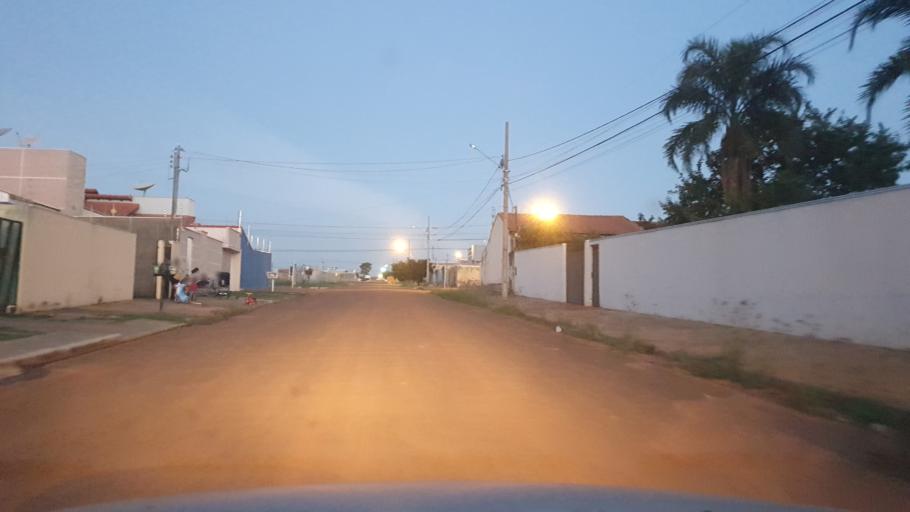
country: BR
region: Mato Grosso
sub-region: Pontes E Lacerda
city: Pontes e Lacerda
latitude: -15.2476
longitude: -59.3241
